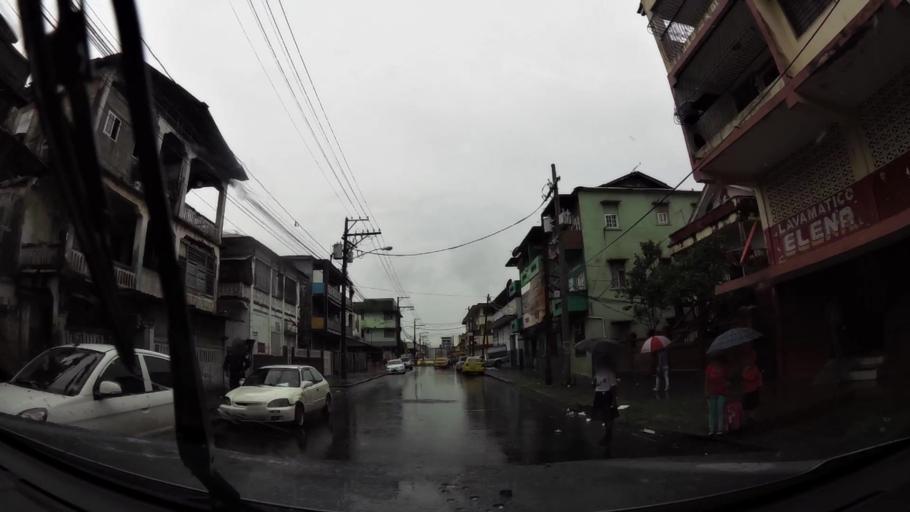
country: PA
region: Colon
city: Colon
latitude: 9.3590
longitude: -79.8998
